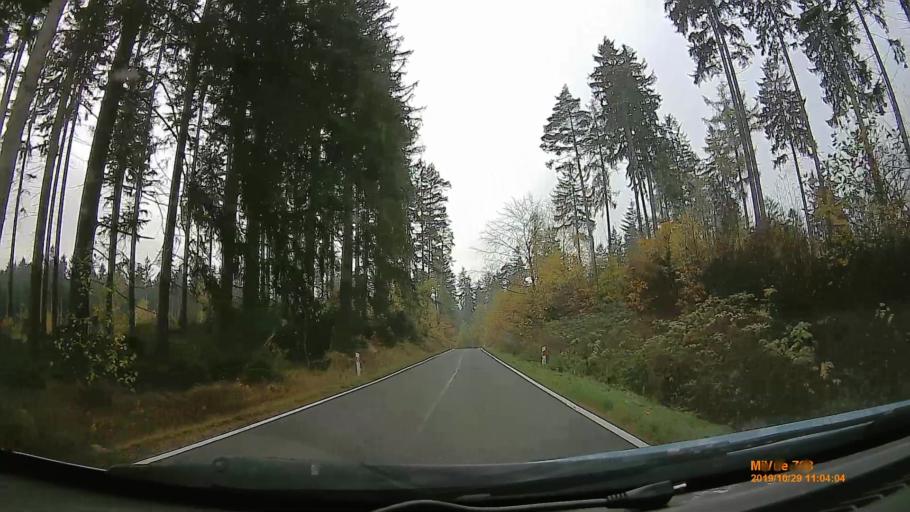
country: PL
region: Lower Silesian Voivodeship
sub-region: Powiat klodzki
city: Szczytna
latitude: 50.4801
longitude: 16.4669
